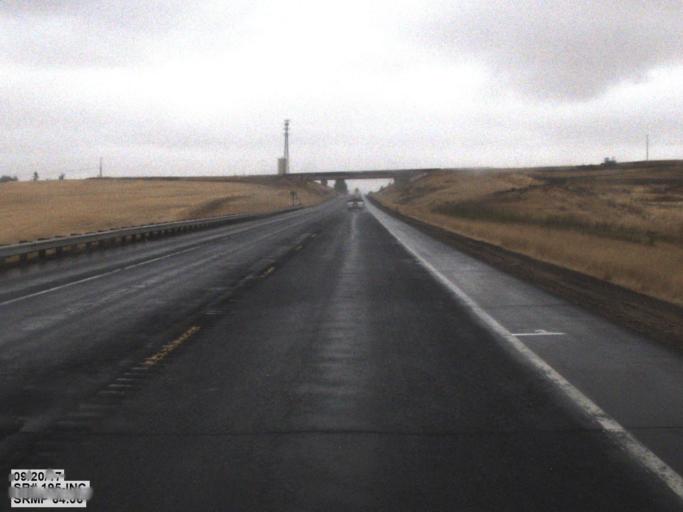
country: US
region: Washington
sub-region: Spokane County
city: Cheney
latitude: 47.2297
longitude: -117.3565
